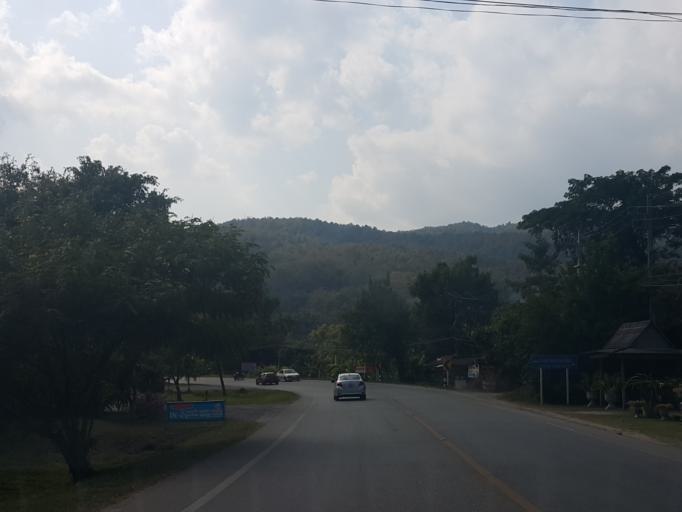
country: TH
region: Chiang Mai
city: Chiang Mai
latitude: 18.9152
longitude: 98.9073
